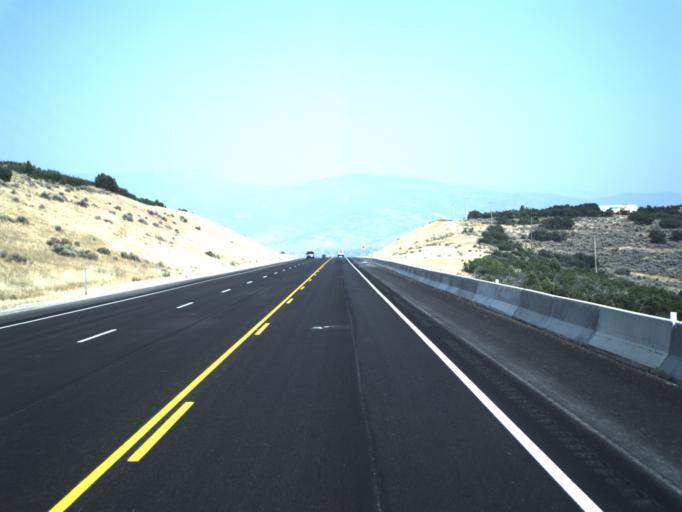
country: US
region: Utah
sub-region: Summit County
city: Kamas
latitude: 40.6351
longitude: -111.3423
